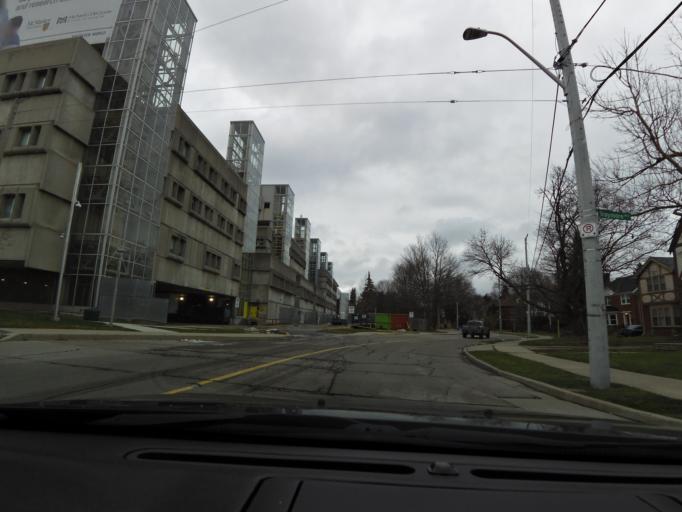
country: CA
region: Ontario
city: Hamilton
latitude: 43.2586
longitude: -79.9161
